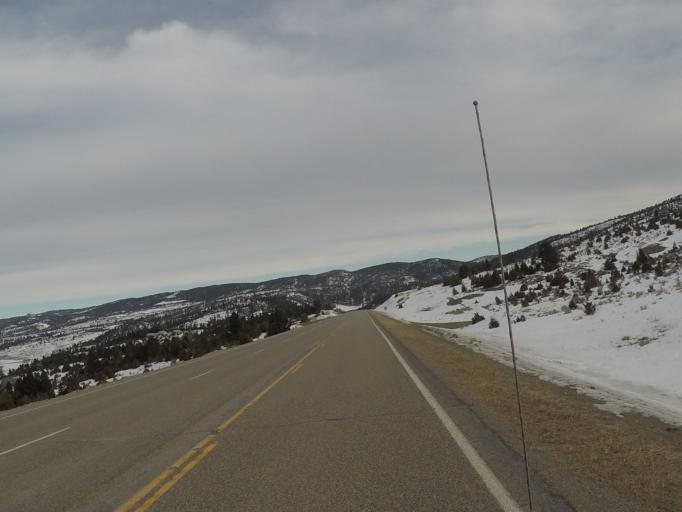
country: US
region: Montana
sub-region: Meagher County
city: White Sulphur Springs
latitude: 46.6548
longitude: -110.8721
